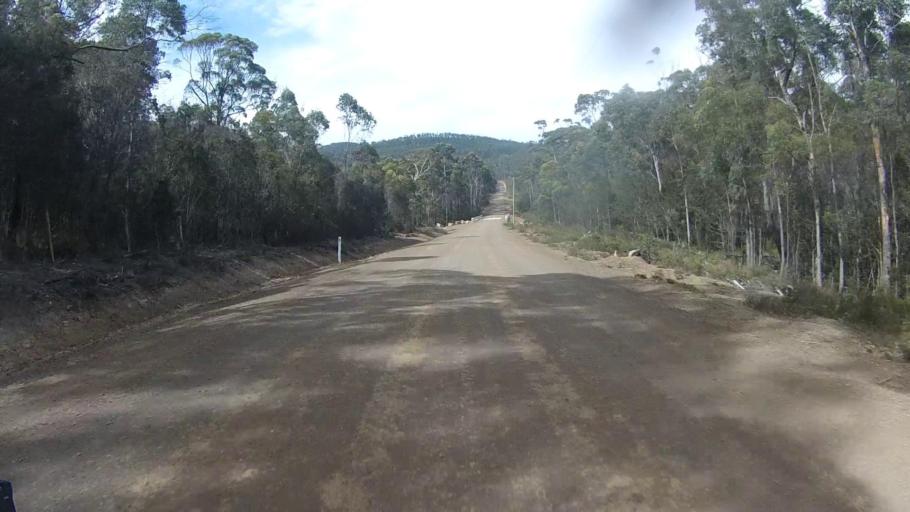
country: AU
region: Tasmania
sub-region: Sorell
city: Sorell
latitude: -42.6776
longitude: 147.8834
